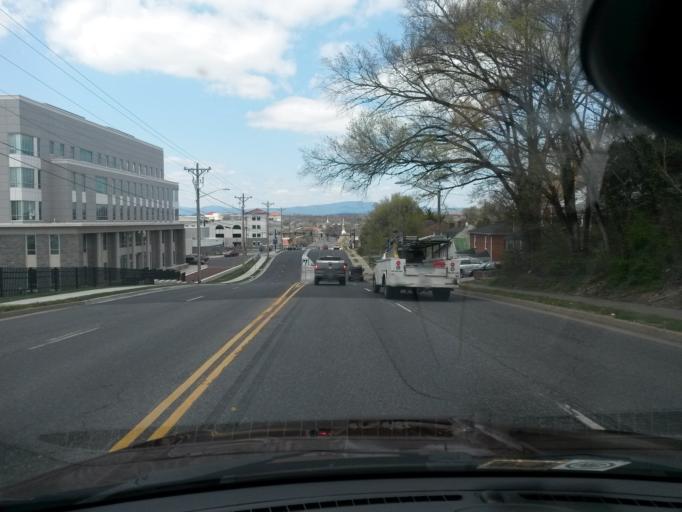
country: US
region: Virginia
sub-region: City of Harrisonburg
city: Harrisonburg
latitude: 38.4400
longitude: -78.8692
